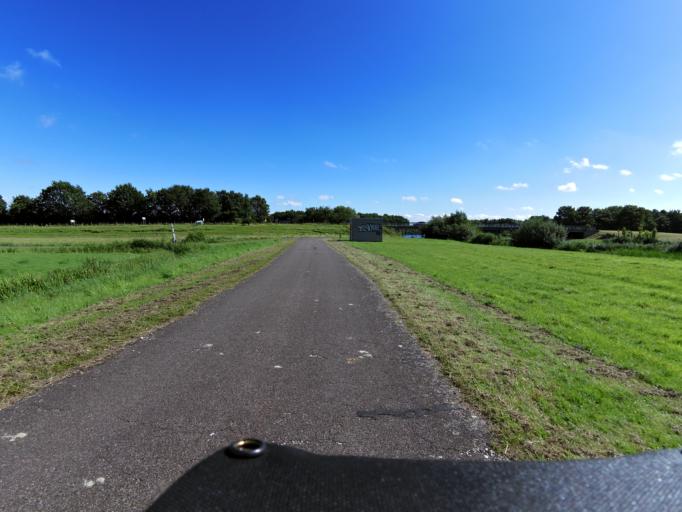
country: NL
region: South Holland
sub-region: Gemeente Spijkenisse
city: Spijkenisse
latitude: 51.8260
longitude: 4.2668
